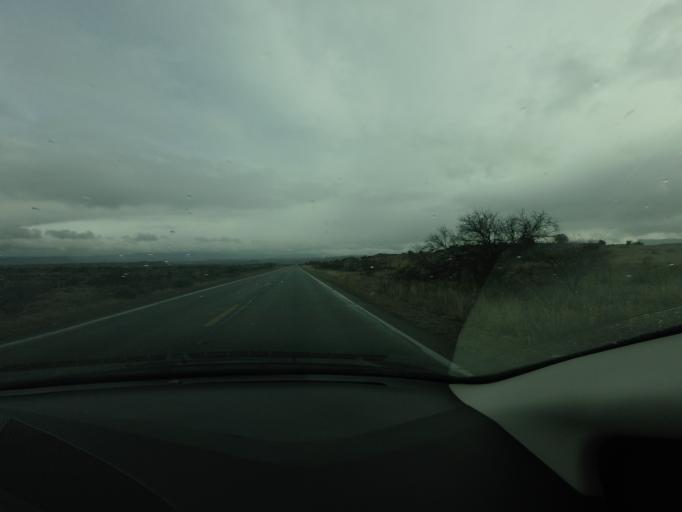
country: US
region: Arizona
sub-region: Yavapai County
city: Lake Montezuma
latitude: 34.6810
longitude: -111.8435
